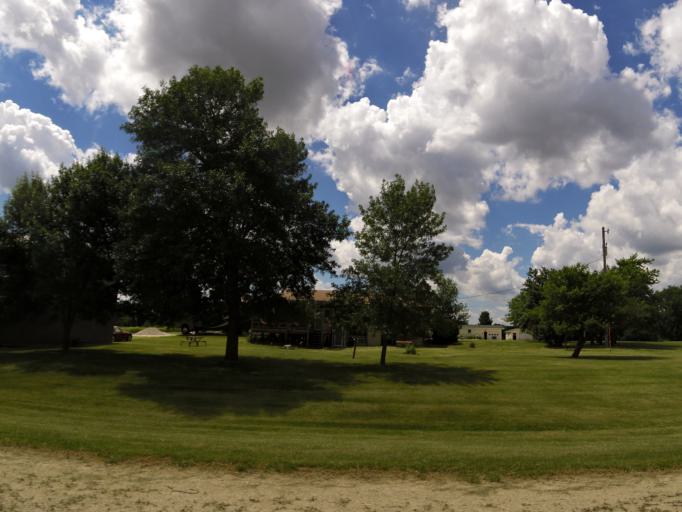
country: US
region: Iowa
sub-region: Fayette County
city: Oelwein
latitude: 42.6065
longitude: -91.9033
